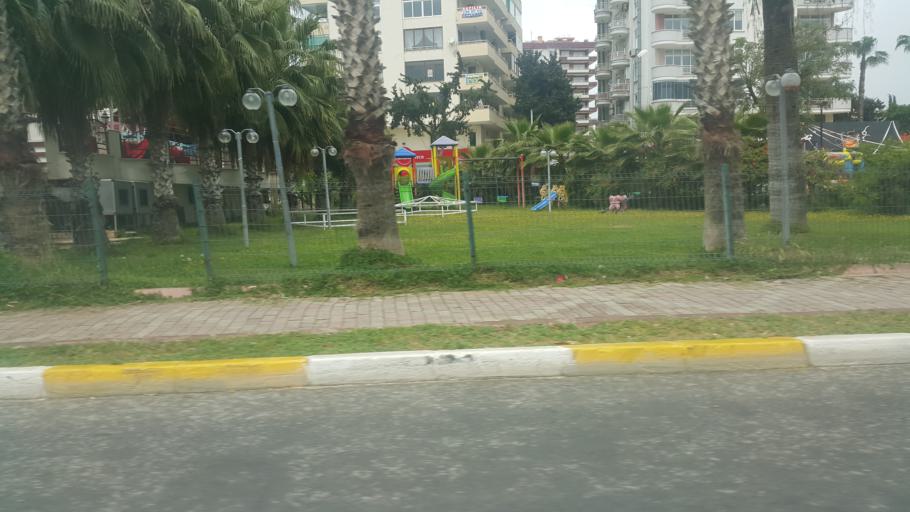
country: TR
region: Mersin
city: Mercin
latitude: 36.7695
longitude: 34.5631
